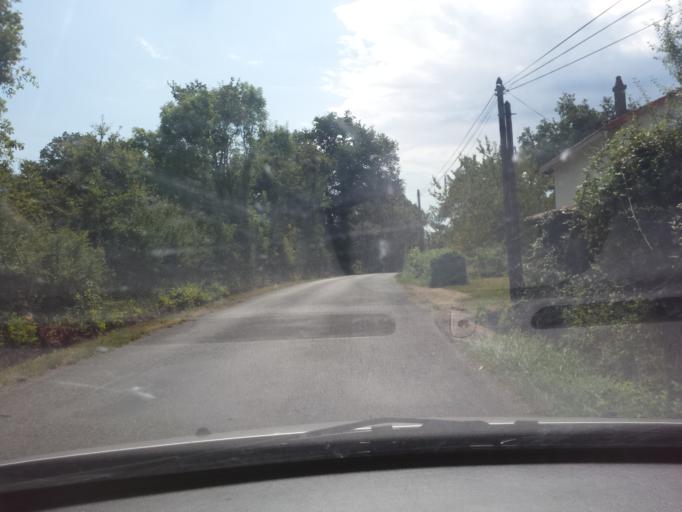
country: FR
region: Poitou-Charentes
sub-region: Departement de la Vienne
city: Availles-Limouzine
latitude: 46.1069
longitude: 0.6965
